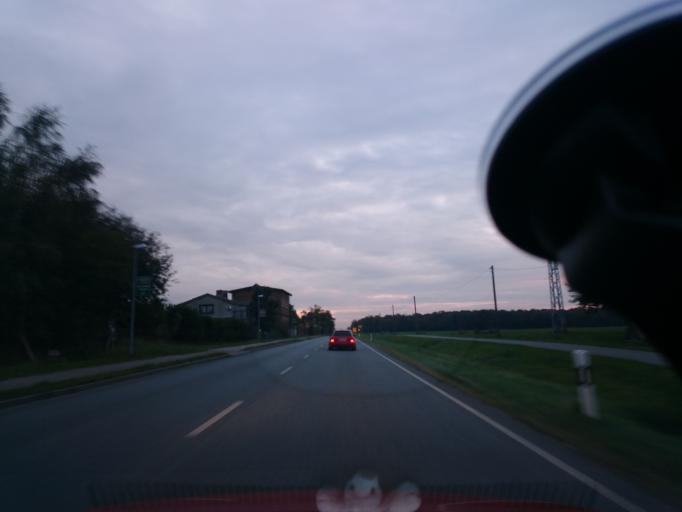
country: DE
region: Mecklenburg-Vorpommern
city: Monchhagen
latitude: 54.1460
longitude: 12.2261
